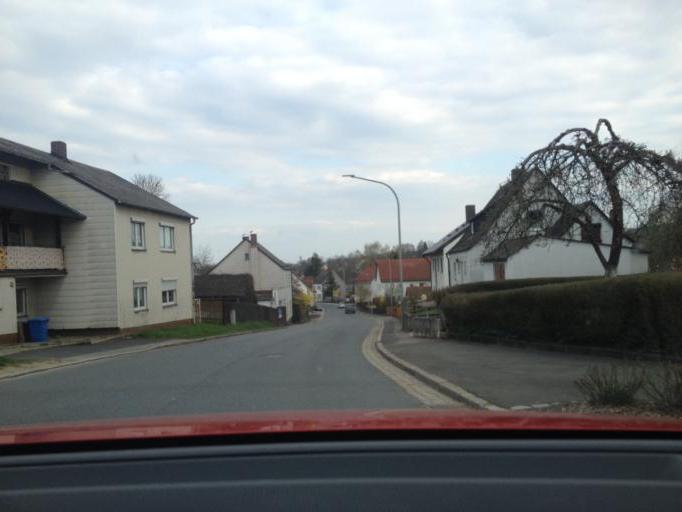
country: DE
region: Bavaria
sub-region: Upper Palatinate
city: Speinshart
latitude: 49.7565
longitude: 11.8298
